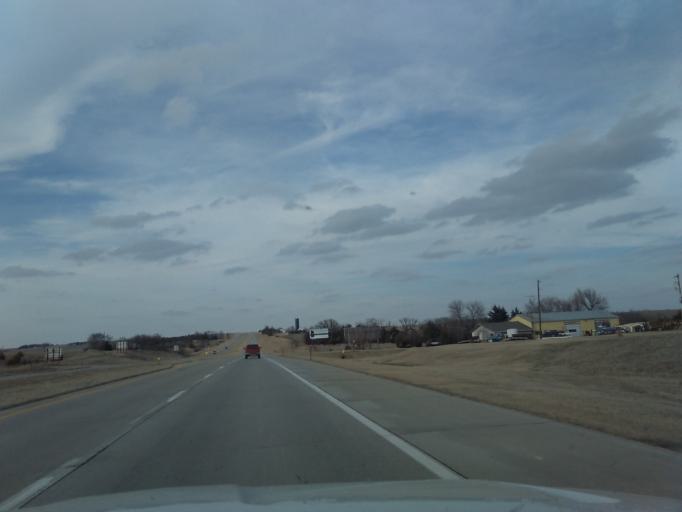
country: US
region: Nebraska
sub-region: Gage County
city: Beatrice
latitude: 40.3841
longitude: -96.7424
